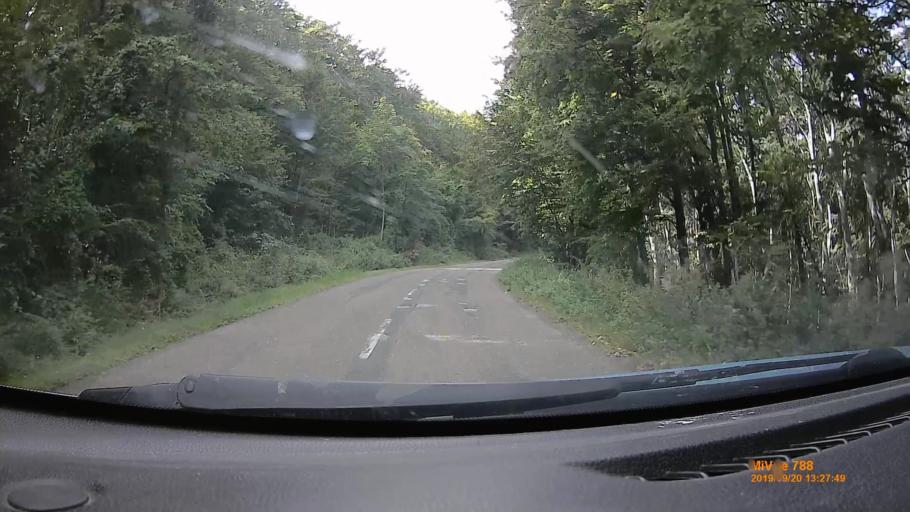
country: HU
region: Heves
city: Szilvasvarad
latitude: 48.0440
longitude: 20.4920
